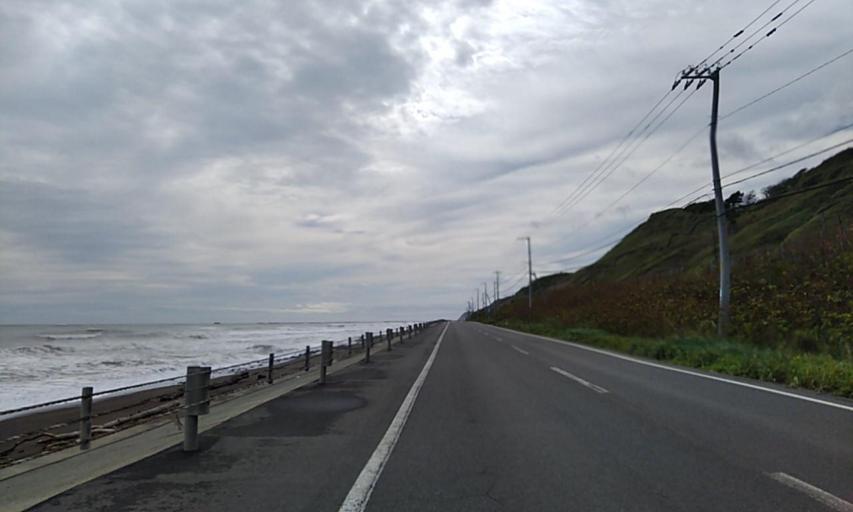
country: JP
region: Hokkaido
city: Kushiro
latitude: 42.8207
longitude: 143.8378
